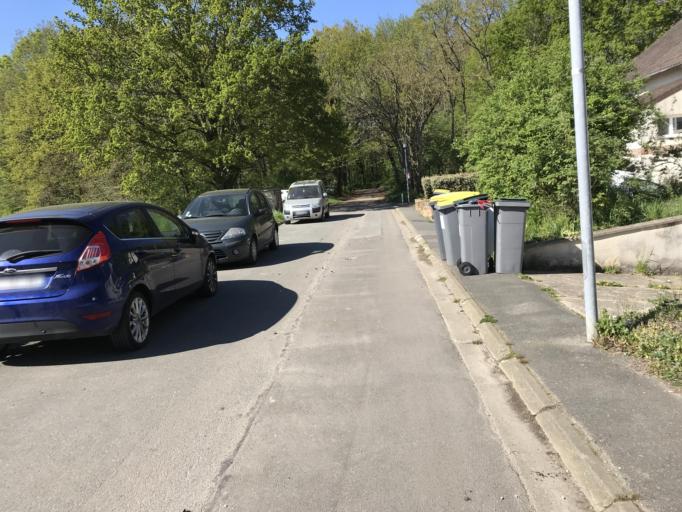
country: FR
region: Ile-de-France
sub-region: Departement de l'Essonne
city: Villejust
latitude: 48.6864
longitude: 2.2385
